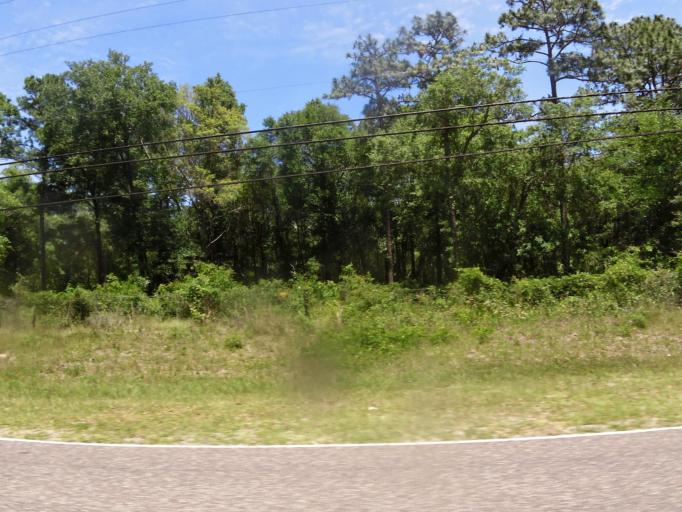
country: US
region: Florida
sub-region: Duval County
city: Atlantic Beach
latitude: 30.4580
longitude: -81.5200
